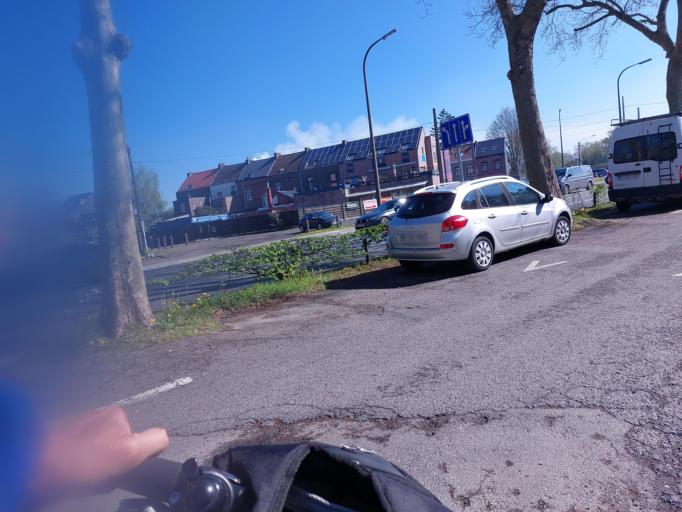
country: BE
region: Wallonia
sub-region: Province du Hainaut
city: Mons
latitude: 50.4531
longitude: 3.9672
